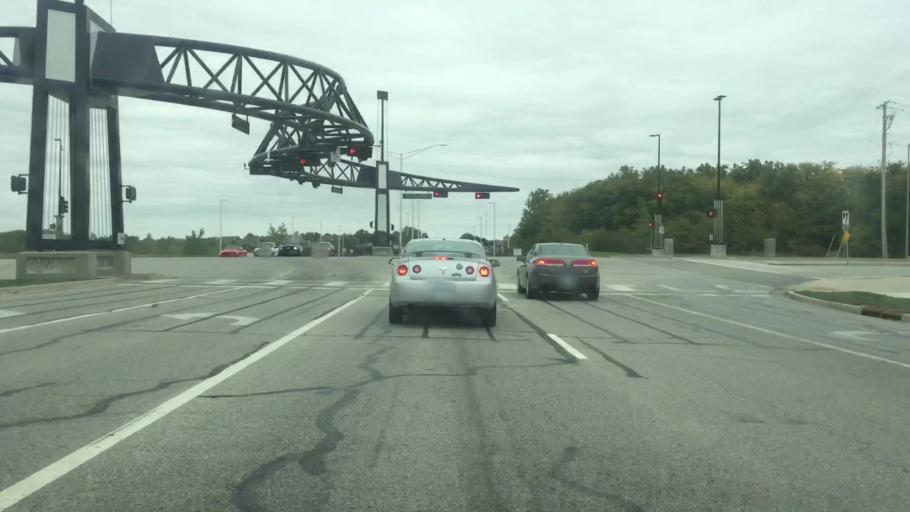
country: US
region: Kansas
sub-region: Johnson County
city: Lenexa
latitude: 38.9705
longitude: -94.7797
